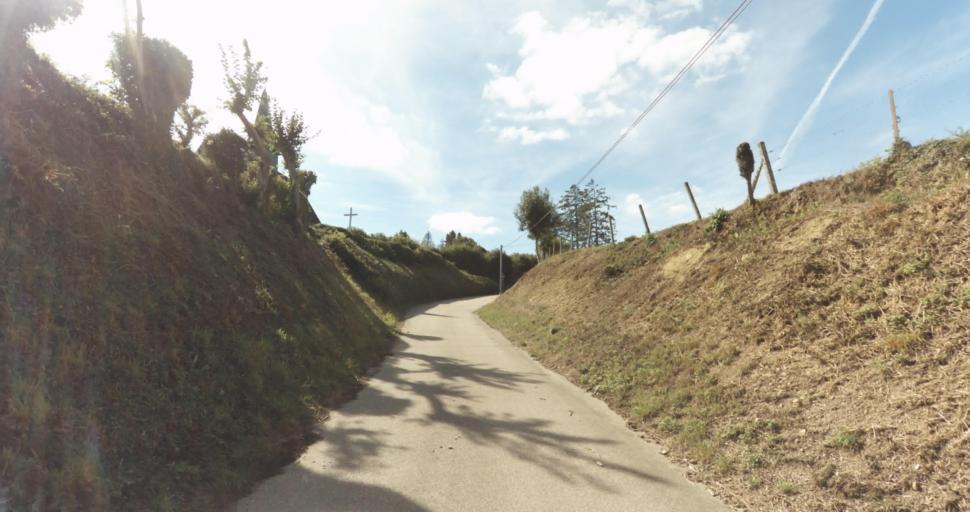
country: FR
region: Lower Normandy
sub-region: Departement de l'Orne
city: Vimoutiers
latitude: 48.9124
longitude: 0.1916
